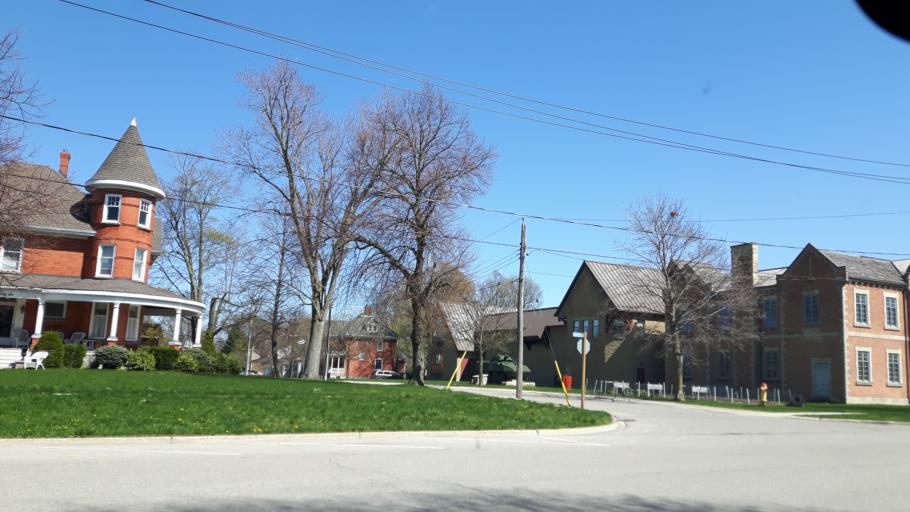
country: CA
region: Ontario
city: Goderich
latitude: 43.7473
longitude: -81.7114
